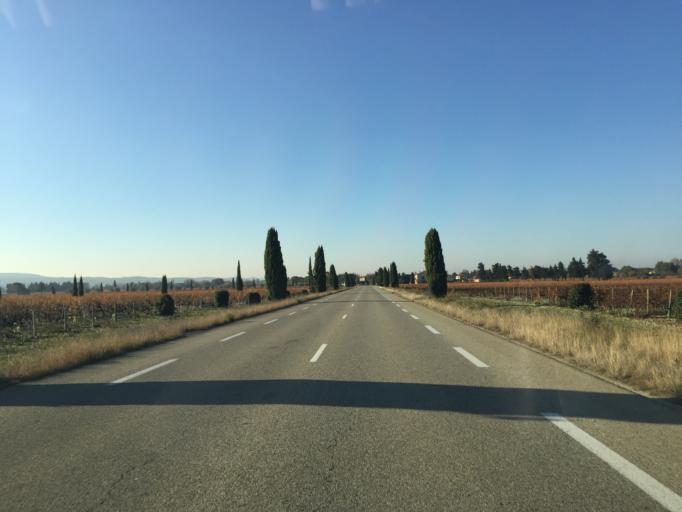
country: FR
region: Provence-Alpes-Cote d'Azur
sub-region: Departement du Vaucluse
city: Sainte-Cecile-les-Vignes
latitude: 44.2410
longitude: 4.9033
